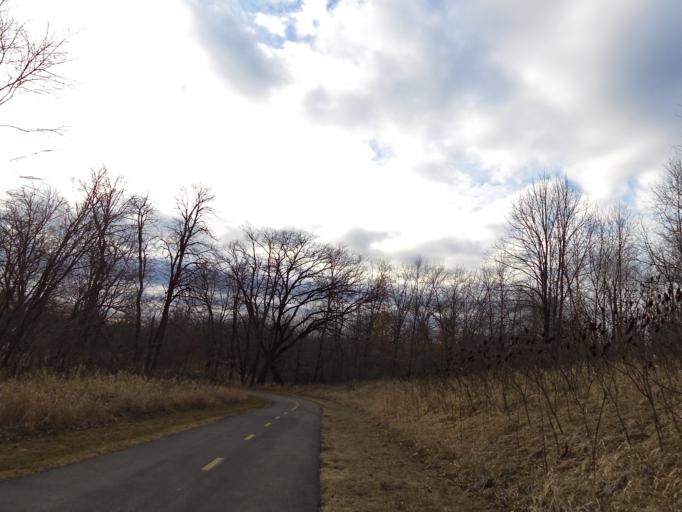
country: US
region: Minnesota
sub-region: Scott County
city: Prior Lake
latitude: 44.6956
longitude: -93.3887
